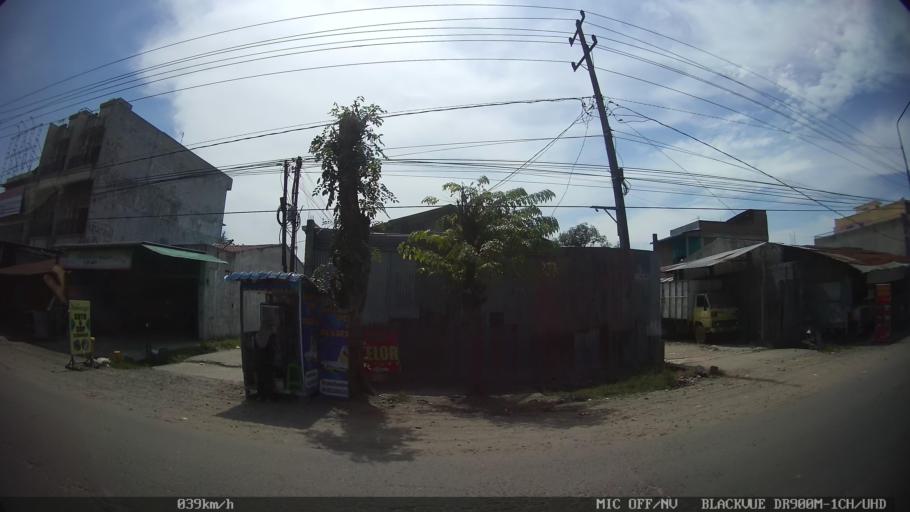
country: ID
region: North Sumatra
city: Labuhan Deli
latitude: 3.6858
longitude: 98.6561
